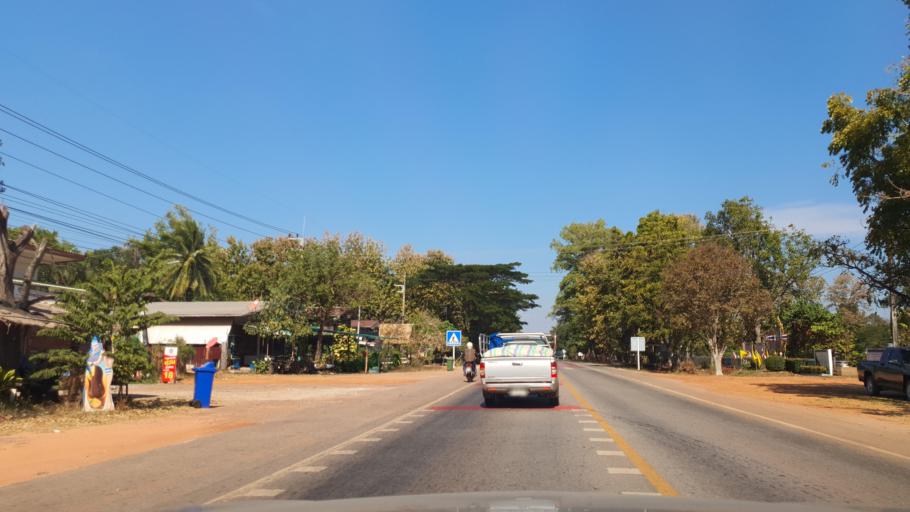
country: TH
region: Sakon Nakhon
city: Phu Phan
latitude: 17.0817
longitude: 103.9810
